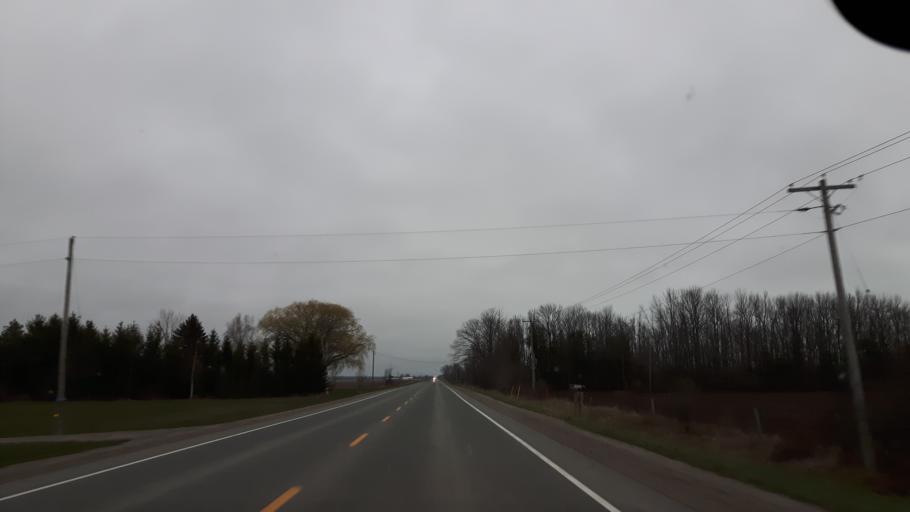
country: CA
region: Ontario
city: Goderich
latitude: 43.6518
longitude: -81.7057
